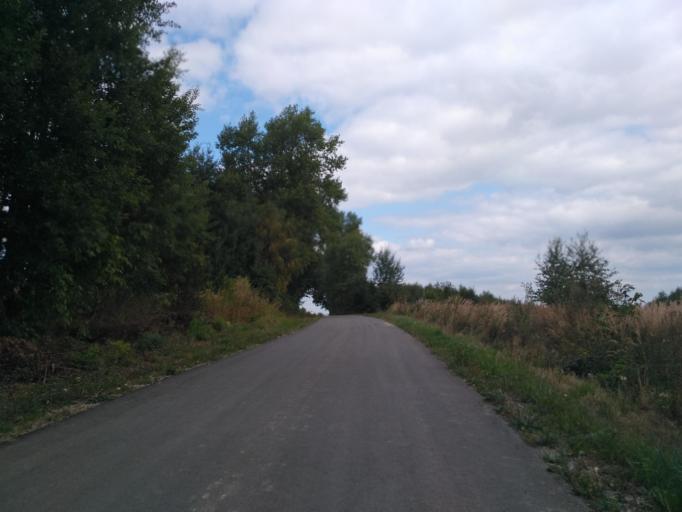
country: PL
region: Subcarpathian Voivodeship
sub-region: Powiat rzeszowski
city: Dynow
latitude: 49.7801
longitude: 22.2794
